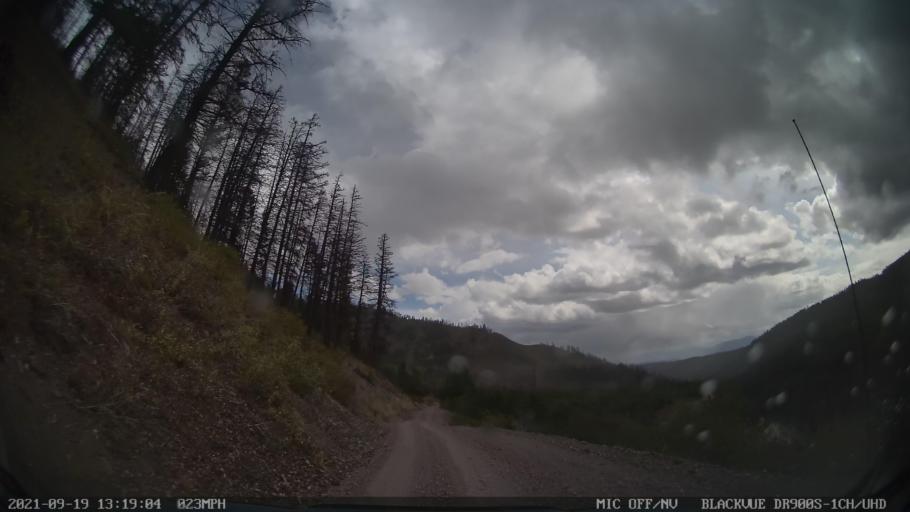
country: US
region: Montana
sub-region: Missoula County
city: Seeley Lake
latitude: 47.1696
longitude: -113.3522
